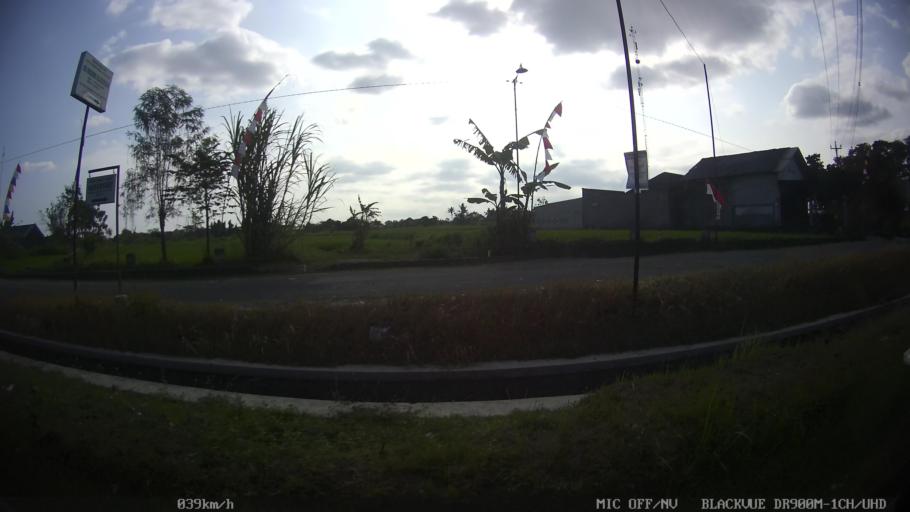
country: ID
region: Central Java
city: Candi Prambanan
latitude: -7.7202
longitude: 110.4729
